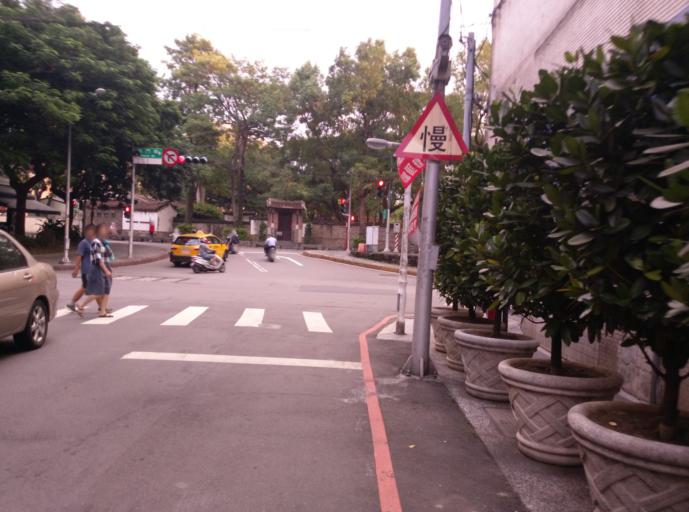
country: TW
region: Taipei
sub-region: Taipei
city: Banqiao
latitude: 25.0117
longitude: 121.4552
